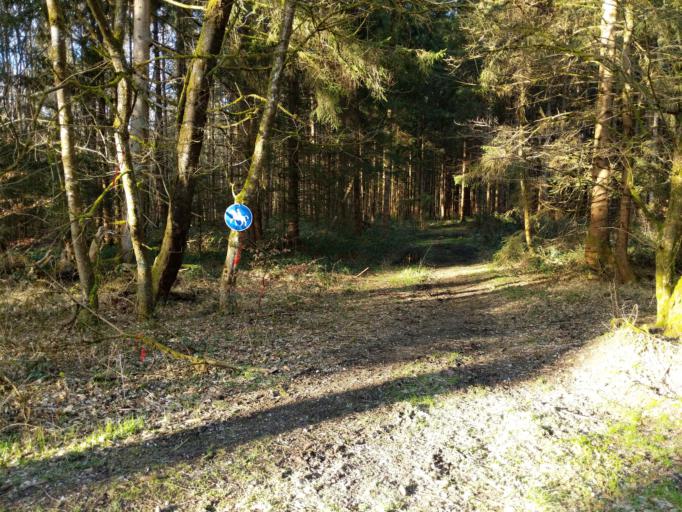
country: DE
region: Bavaria
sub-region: Upper Bavaria
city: Zorneding
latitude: 48.1013
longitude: 11.8457
